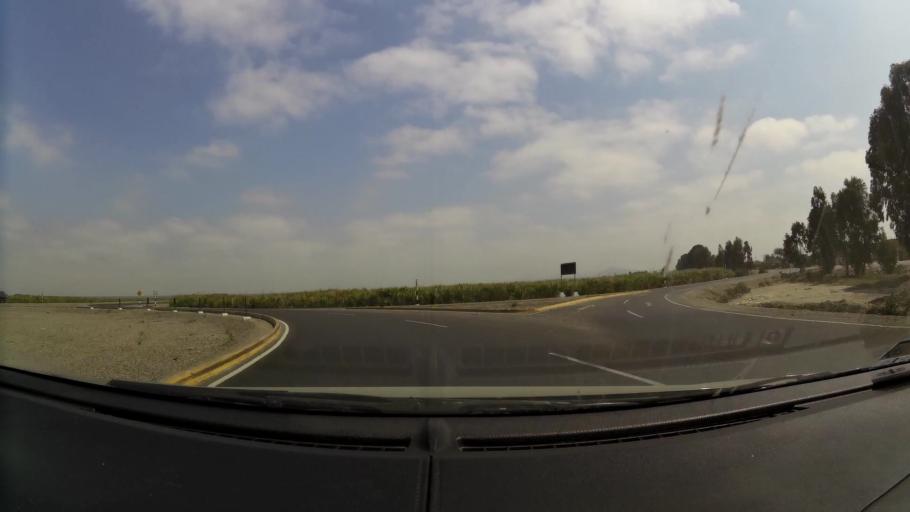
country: PE
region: La Libertad
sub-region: Ascope
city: Chicama
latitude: -7.8610
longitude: -79.1405
